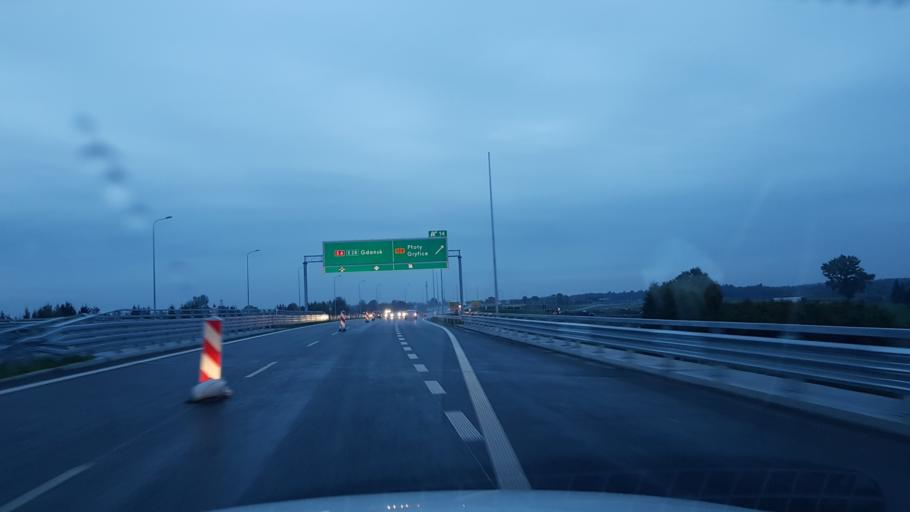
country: PL
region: West Pomeranian Voivodeship
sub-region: Powiat gryficki
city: Ploty
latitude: 53.8150
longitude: 15.2497
